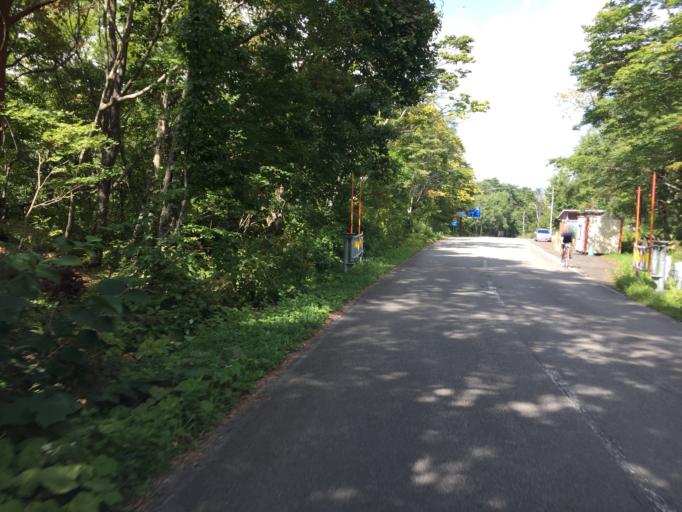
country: JP
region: Fukushima
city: Inawashiro
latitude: 37.6424
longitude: 140.0503
